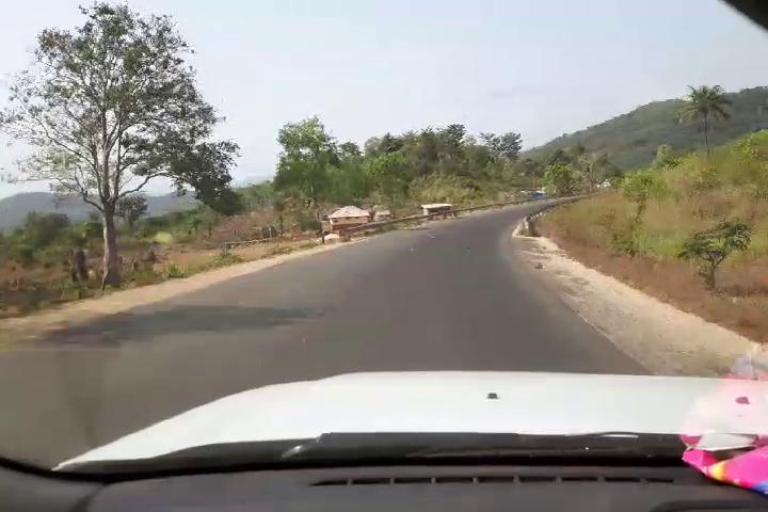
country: SL
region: Western Area
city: Waterloo
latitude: 8.2700
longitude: -13.1588
